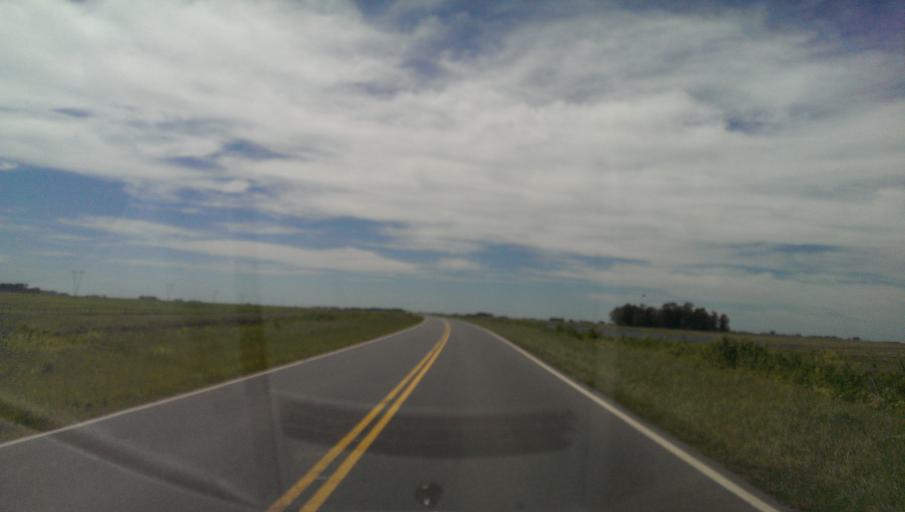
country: AR
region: Buenos Aires
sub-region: Partido de Laprida
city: Laprida
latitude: -37.2327
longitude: -60.7113
